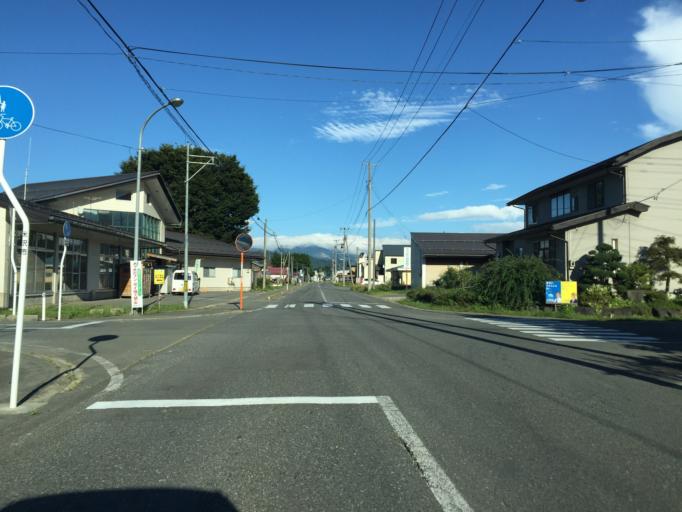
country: JP
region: Yamagata
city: Yonezawa
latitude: 37.8822
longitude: 140.1077
